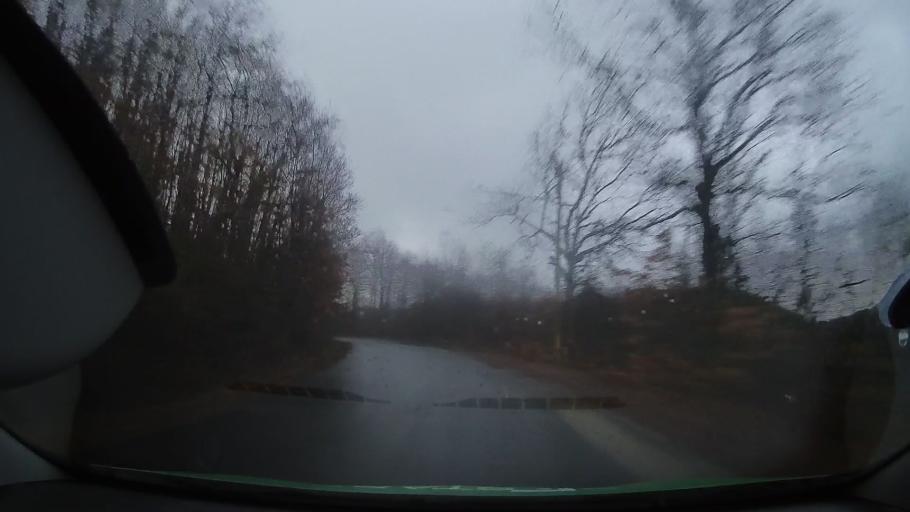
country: RO
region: Hunedoara
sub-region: Comuna Ribita
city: Ribita
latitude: 46.2346
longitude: 22.7485
